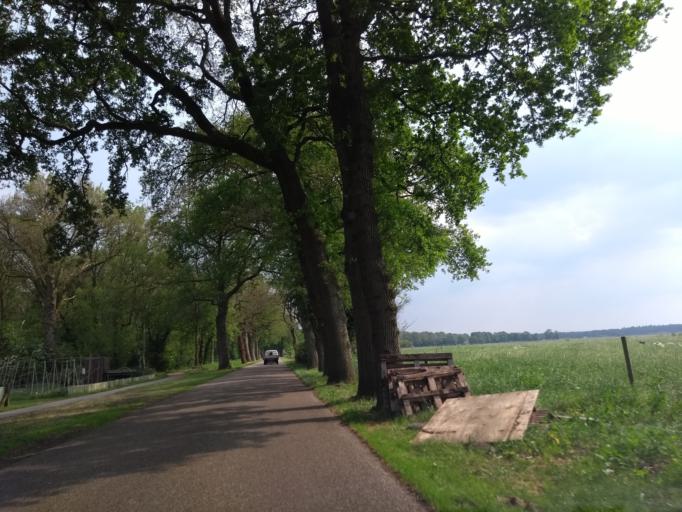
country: NL
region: Overijssel
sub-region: Gemeente Staphorst
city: Staphorst
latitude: 52.6542
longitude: 6.2914
